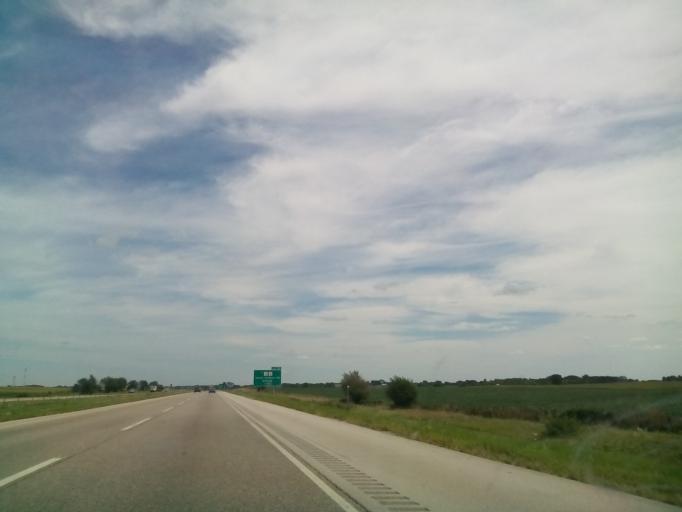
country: US
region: Illinois
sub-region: DeKalb County
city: DeKalb
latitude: 41.9001
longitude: -88.8011
